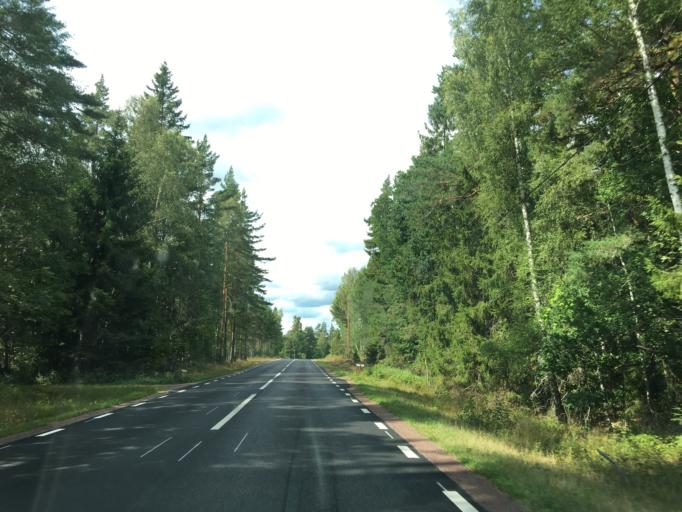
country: SE
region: Kalmar
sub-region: Nybro Kommun
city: Nybro
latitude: 56.9208
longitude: 15.9573
